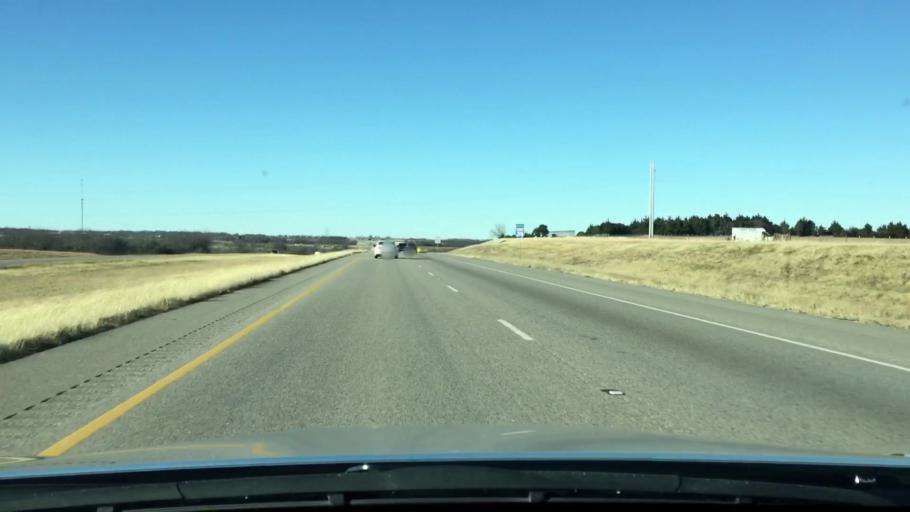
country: US
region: Texas
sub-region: Johnson County
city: Grandview
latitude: 32.2367
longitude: -97.1562
